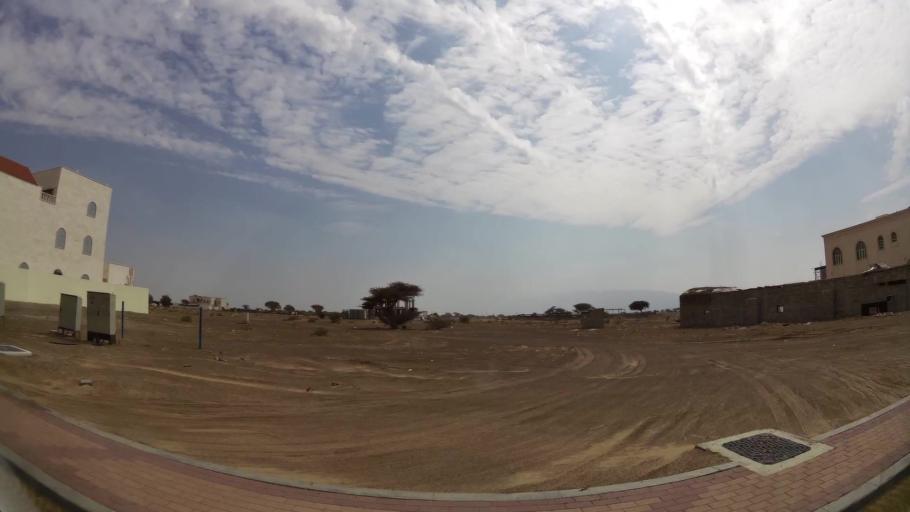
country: AE
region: Abu Dhabi
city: Al Ain
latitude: 24.1868
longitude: 55.8137
